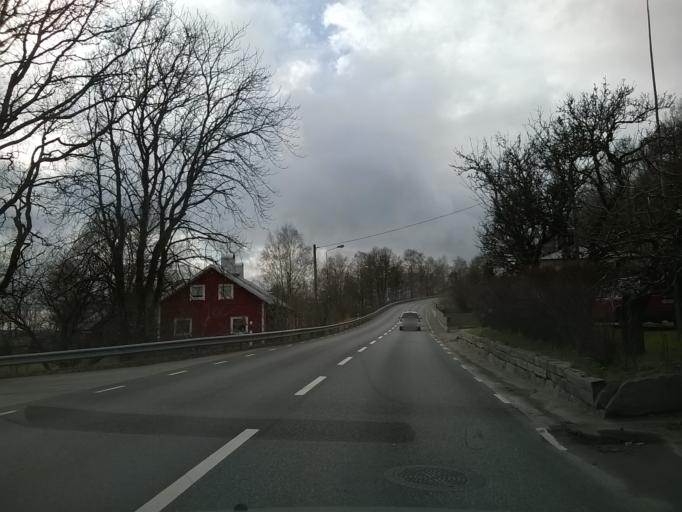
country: SE
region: Halland
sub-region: Varbergs Kommun
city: Tvaaker
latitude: 57.1431
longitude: 12.4661
